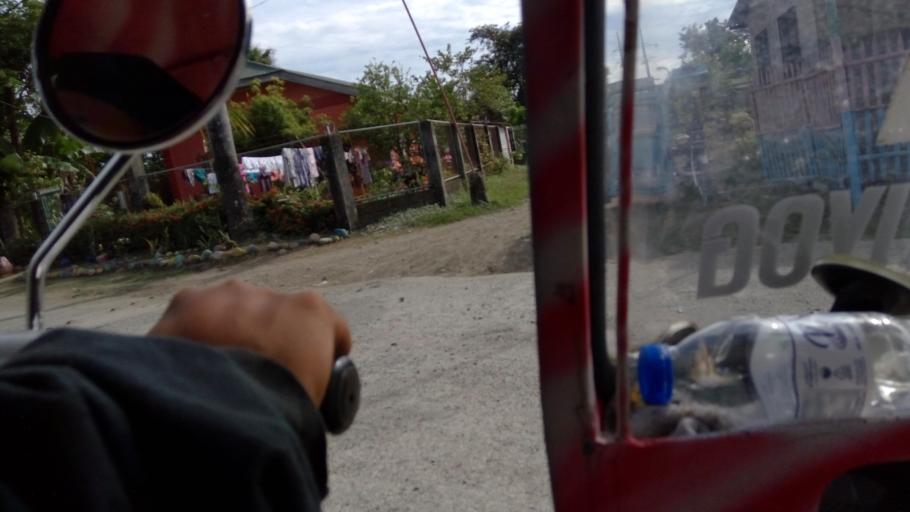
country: PH
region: Ilocos
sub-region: Province of La Union
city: San Eugenio
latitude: 16.3537
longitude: 120.3526
